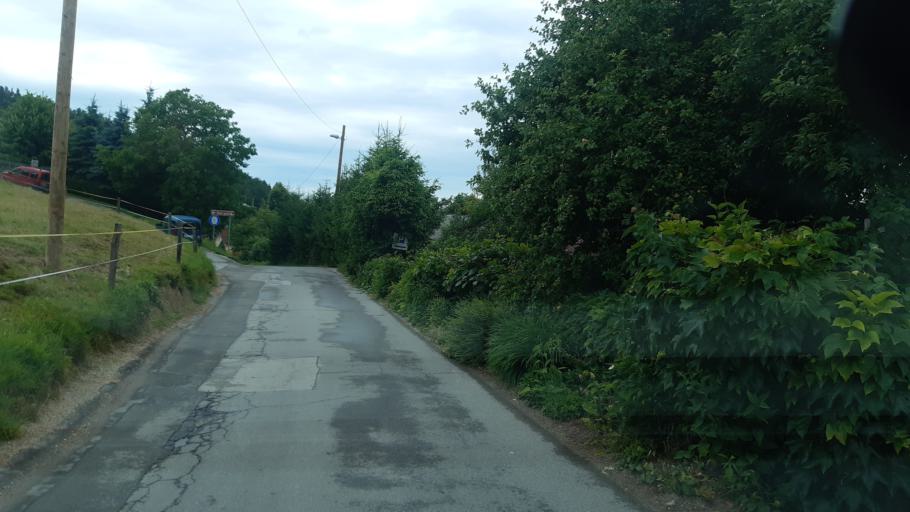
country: SI
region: Medvode
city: Zgornje Pirnice
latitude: 46.1652
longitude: 14.4356
